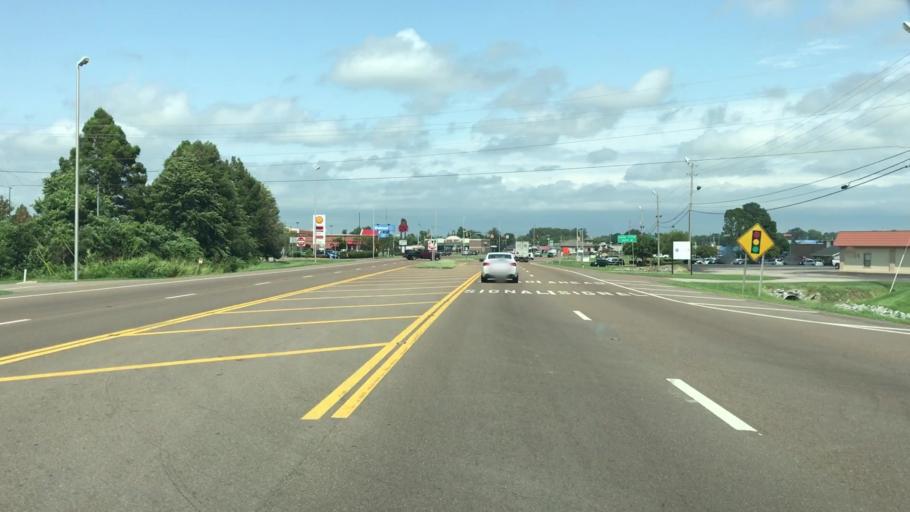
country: US
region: Tennessee
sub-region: Obion County
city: Union City
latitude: 36.4120
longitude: -89.0784
